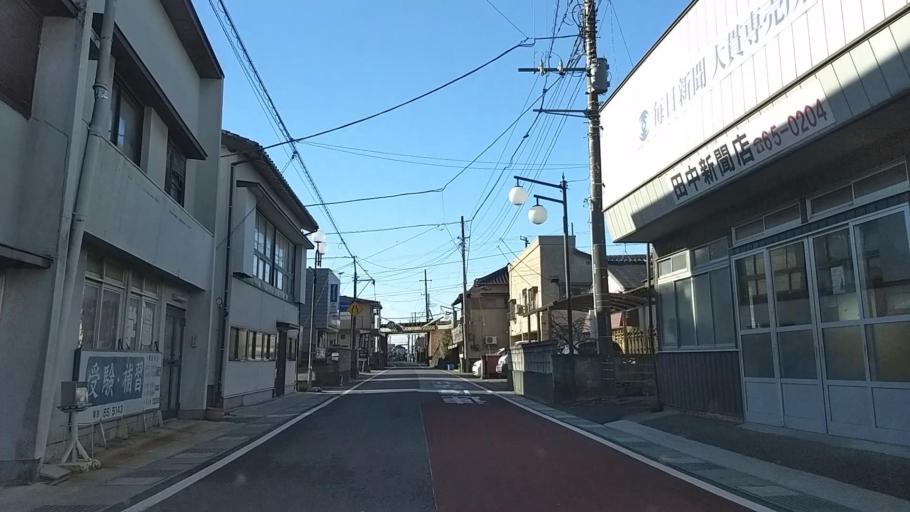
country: JP
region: Chiba
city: Futtsu
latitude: 35.2850
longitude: 139.8582
